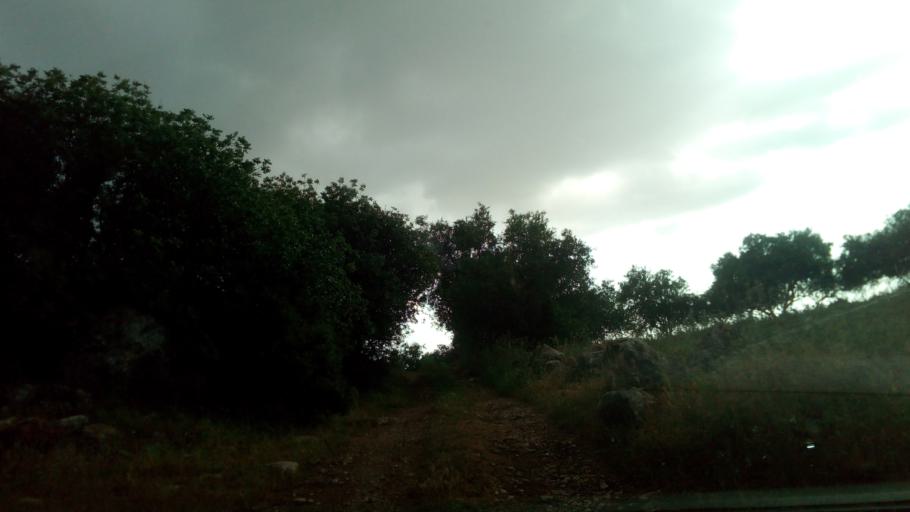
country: CY
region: Pafos
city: Mesogi
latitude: 34.7654
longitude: 32.5628
